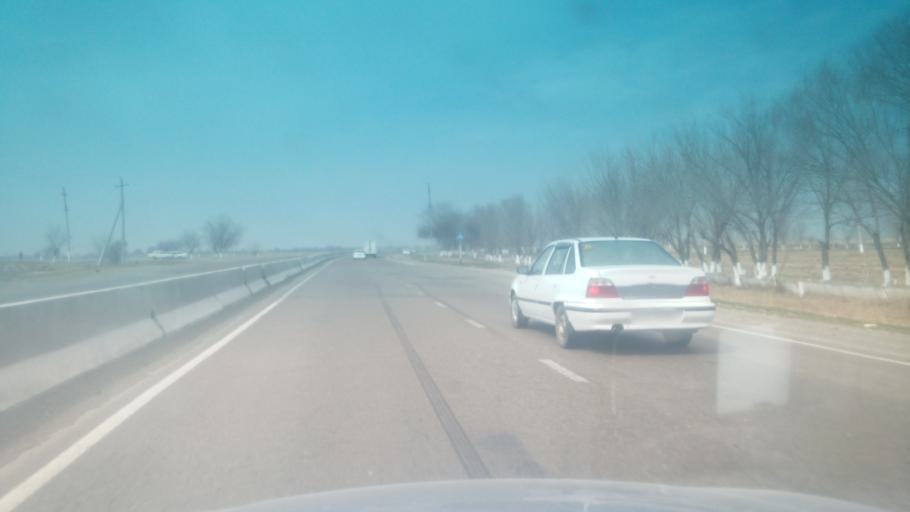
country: KZ
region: Ongtustik Qazaqstan
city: Myrzakent
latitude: 40.5250
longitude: 68.4508
